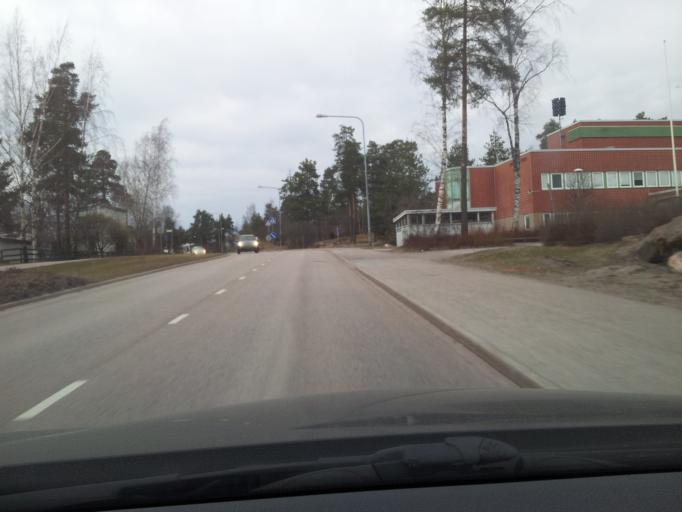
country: FI
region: Uusimaa
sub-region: Helsinki
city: Espoo
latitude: 60.1441
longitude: 24.6561
